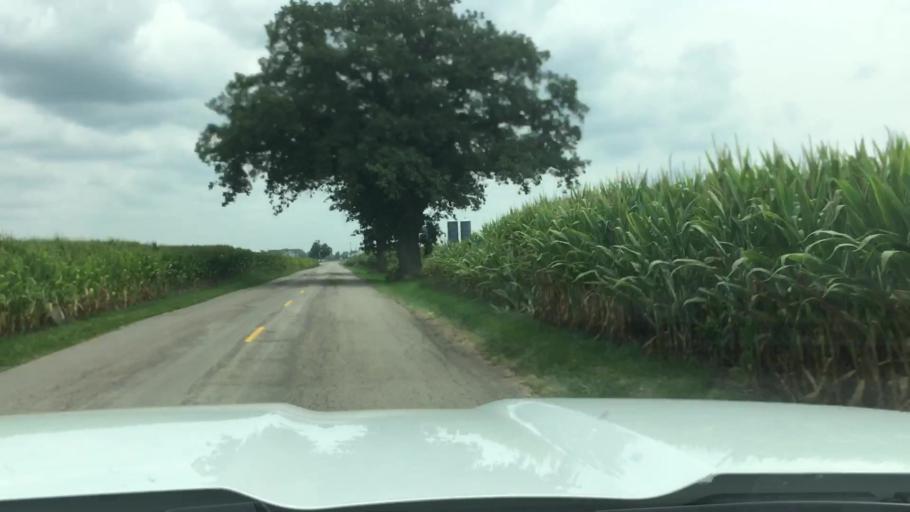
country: US
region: Michigan
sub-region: Ingham County
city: Webberville
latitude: 42.7144
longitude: -84.1806
